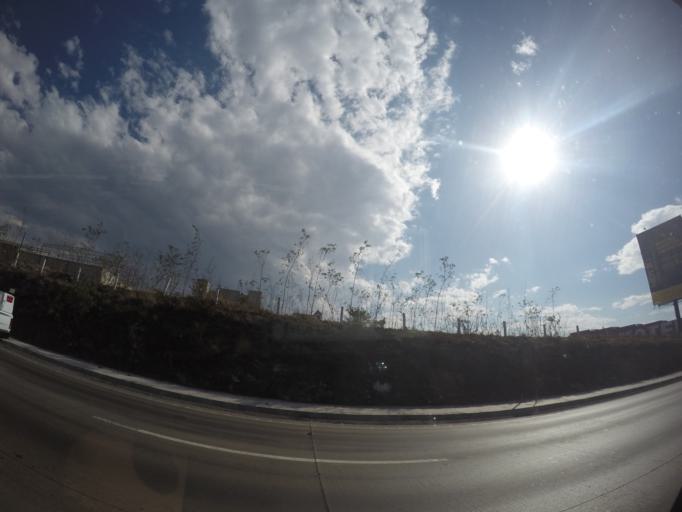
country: MX
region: Queretaro
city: La Canada
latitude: 20.5695
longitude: -100.3043
